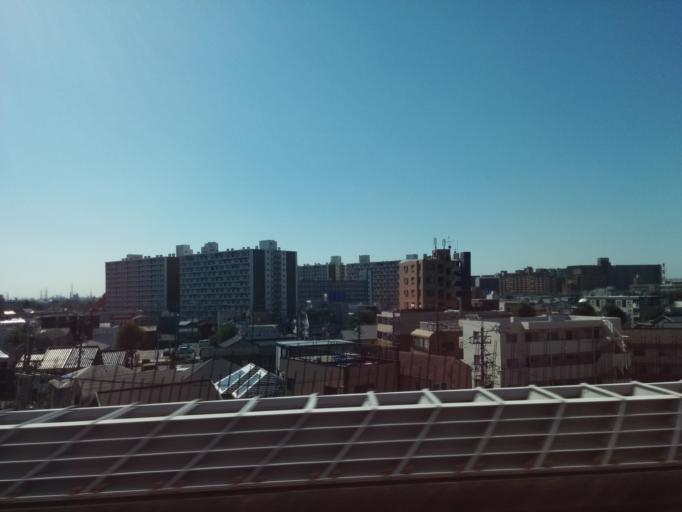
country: JP
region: Aichi
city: Nagoya-shi
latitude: 35.1098
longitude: 136.9083
